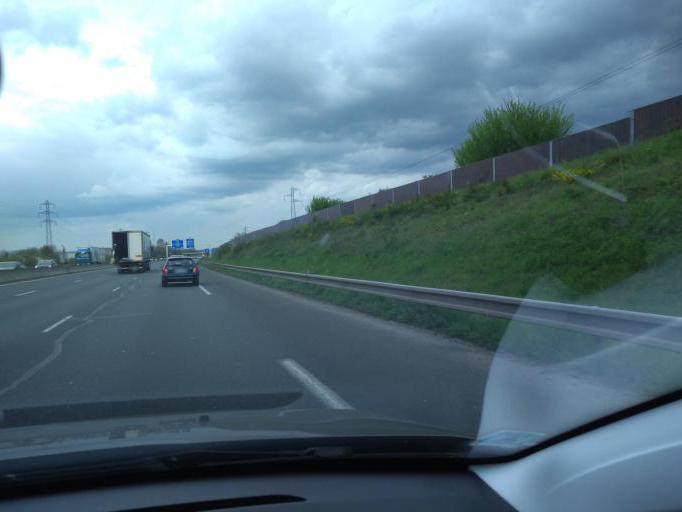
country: FR
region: Pays de la Loire
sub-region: Departement de Maine-et-Loire
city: Ecouflant
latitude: 47.5011
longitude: -0.5081
